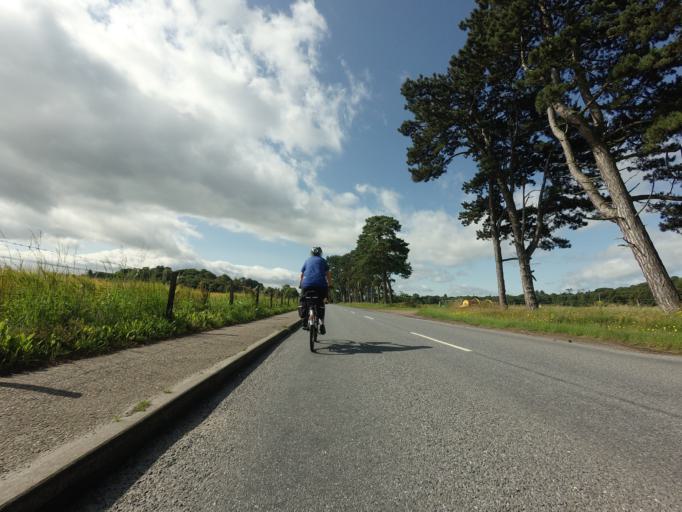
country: GB
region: Scotland
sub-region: Highland
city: Nairn
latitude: 57.5779
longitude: -3.8604
